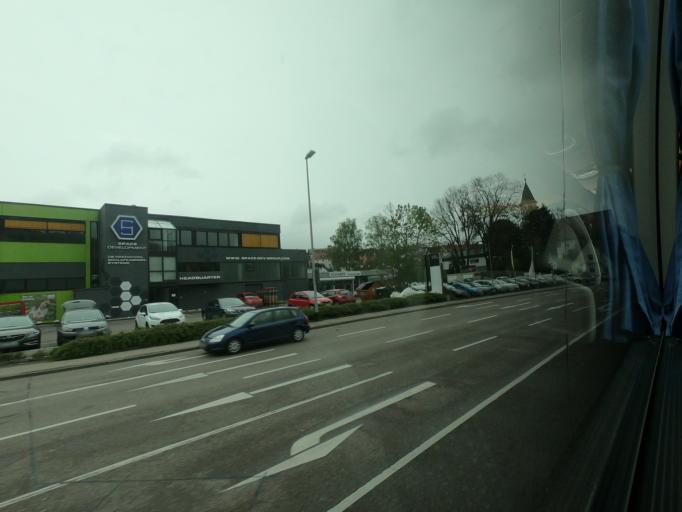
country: DE
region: Baden-Wuerttemberg
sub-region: Regierungsbezirk Stuttgart
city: Heidenheim an der Brenz
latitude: 48.7107
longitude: 10.1612
